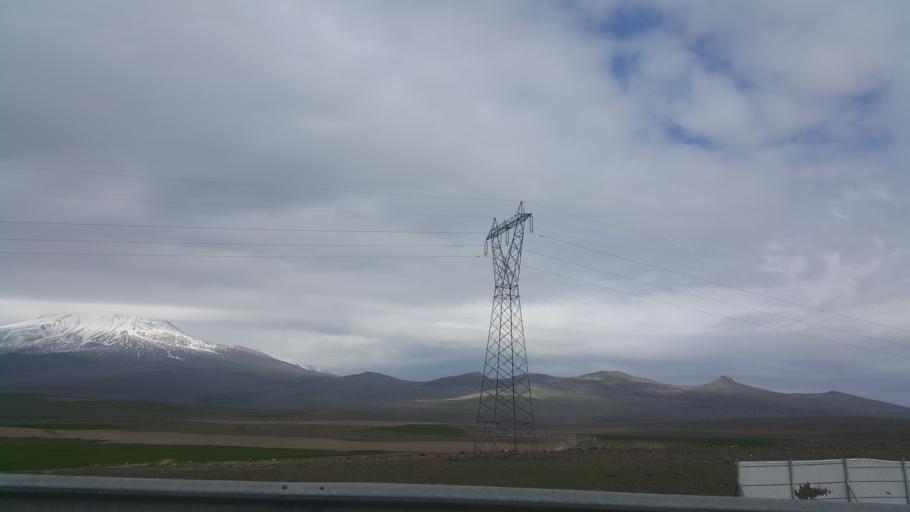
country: TR
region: Aksaray
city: Taspinar
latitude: 38.0829
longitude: 34.0329
